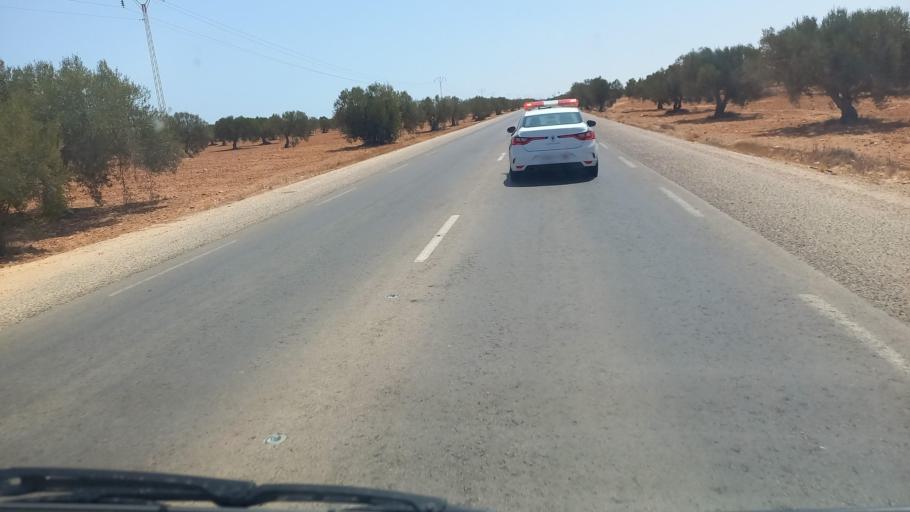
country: TN
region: Madanin
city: Zarzis
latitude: 33.5688
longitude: 11.0451
